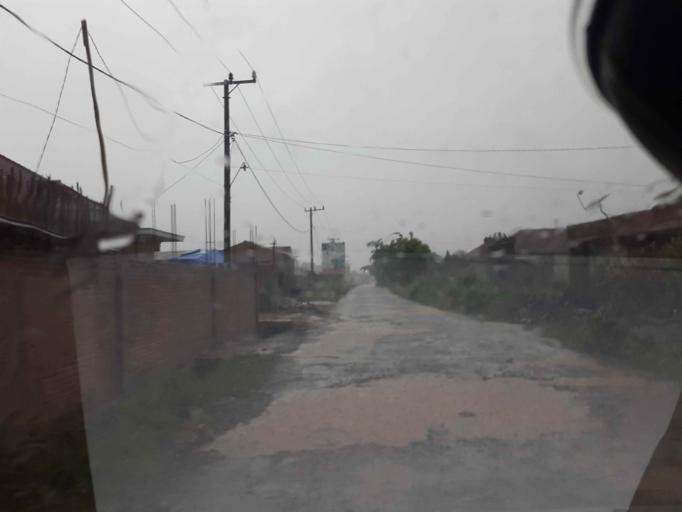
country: ID
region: Lampung
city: Kedaton
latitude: -5.3880
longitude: 105.3161
